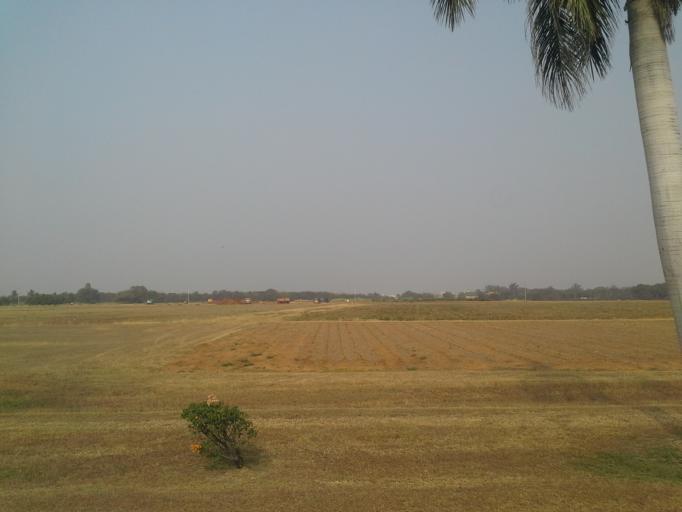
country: IN
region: Telangana
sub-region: Medak
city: Patancheru
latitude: 17.5152
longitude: 78.2762
